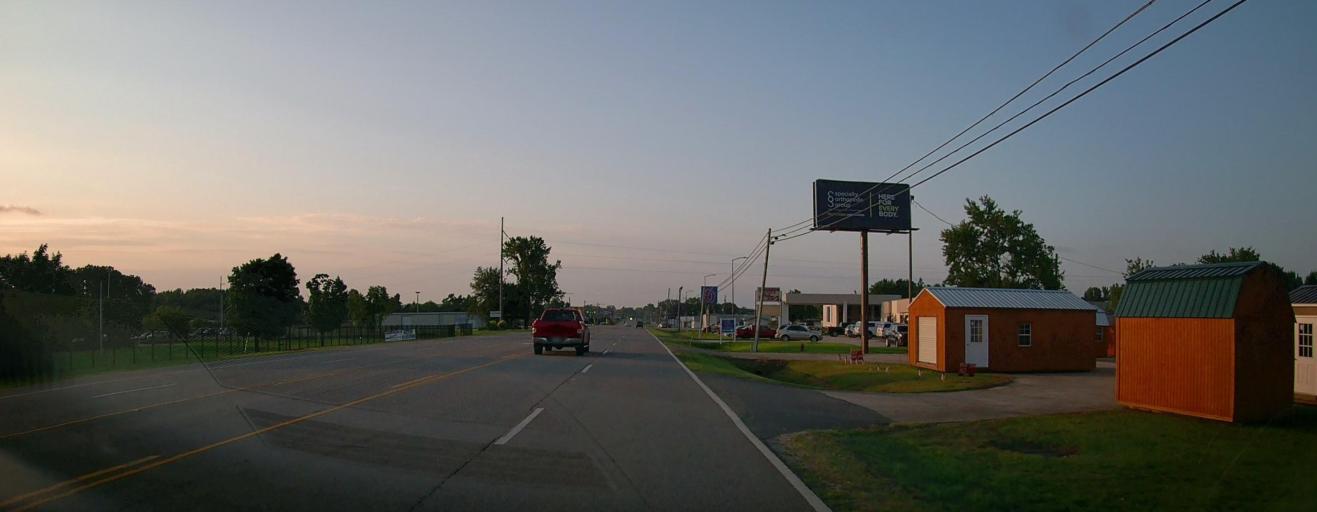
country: US
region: Alabama
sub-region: Marion County
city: Hamilton
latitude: 34.1139
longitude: -87.9893
